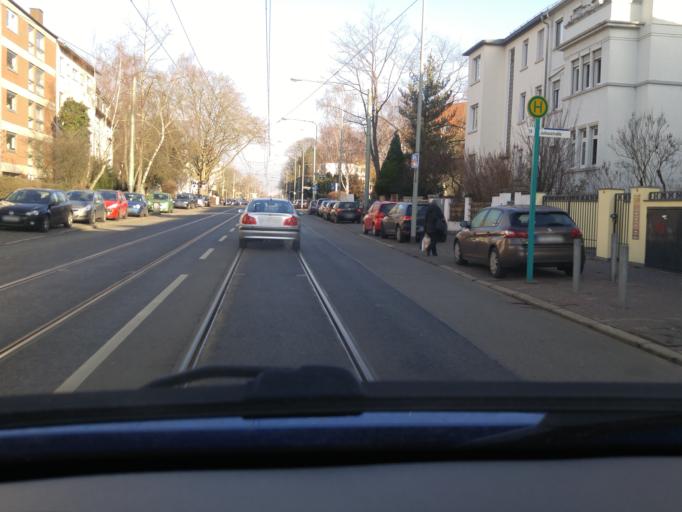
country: DE
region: Hesse
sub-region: Regierungsbezirk Darmstadt
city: Frankfurt am Main
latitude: 50.1256
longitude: 8.6471
